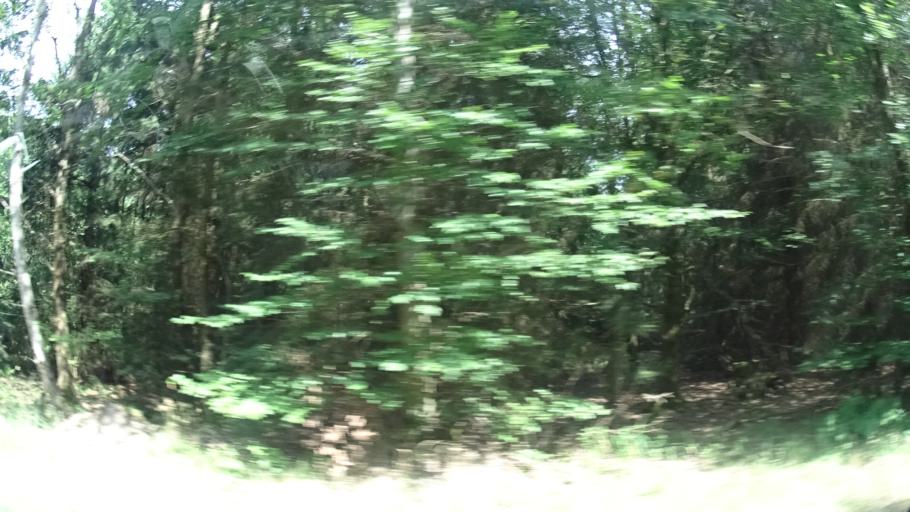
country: DE
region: Hesse
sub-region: Regierungsbezirk Giessen
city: Lauterbach
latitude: 50.5784
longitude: 9.4284
